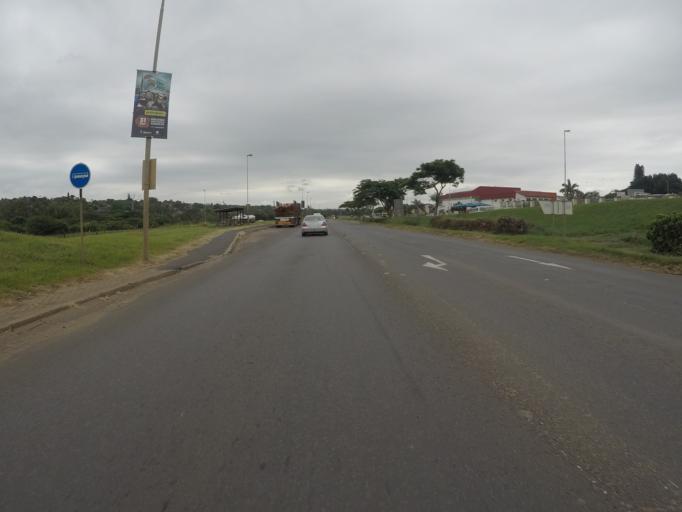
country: ZA
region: KwaZulu-Natal
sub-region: uThungulu District Municipality
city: Empangeni
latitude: -28.7740
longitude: 31.9012
